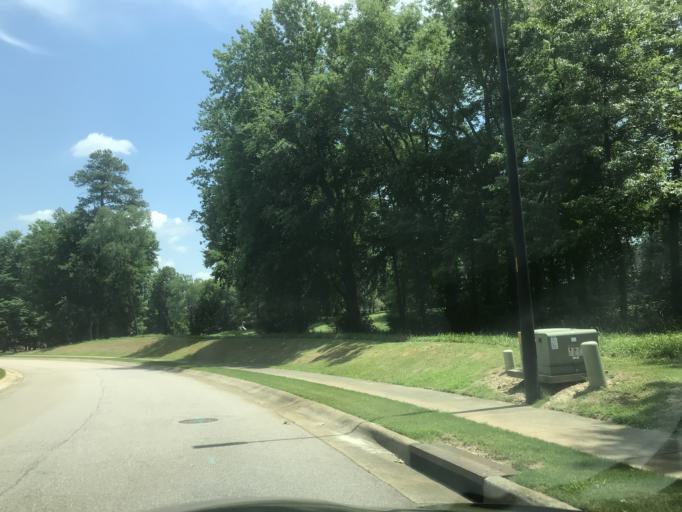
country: US
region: North Carolina
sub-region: Wake County
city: Wake Forest
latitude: 35.9615
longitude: -78.5572
